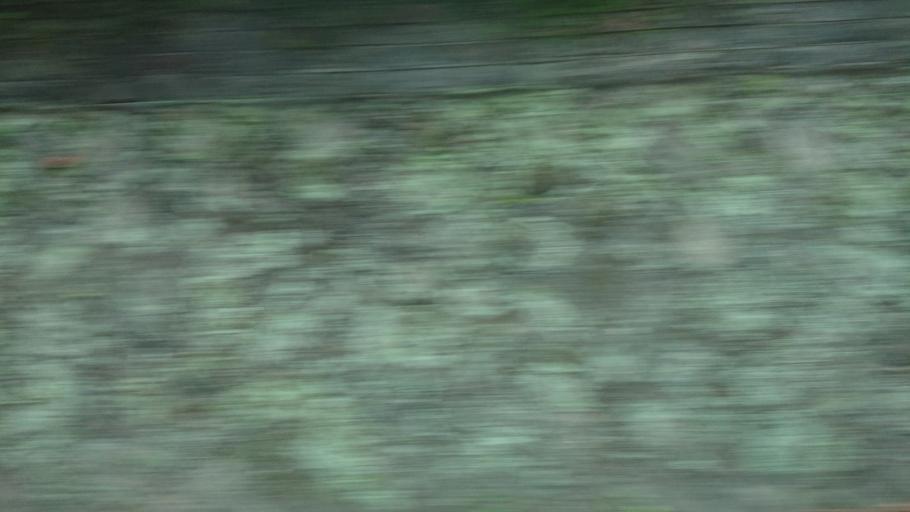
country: TW
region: Taiwan
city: Daxi
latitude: 24.8719
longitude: 121.4051
